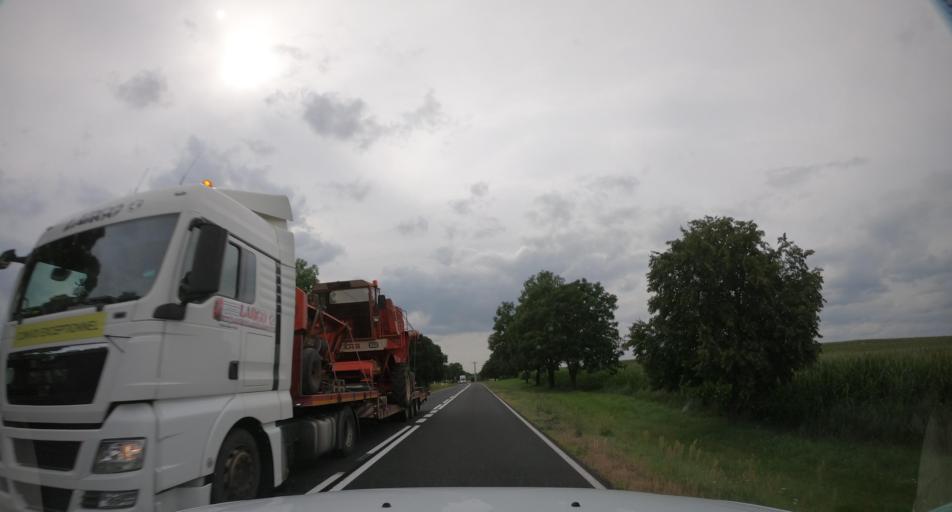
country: PL
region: West Pomeranian Voivodeship
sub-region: Powiat stargardzki
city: Suchan
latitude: 53.2773
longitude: 15.3537
